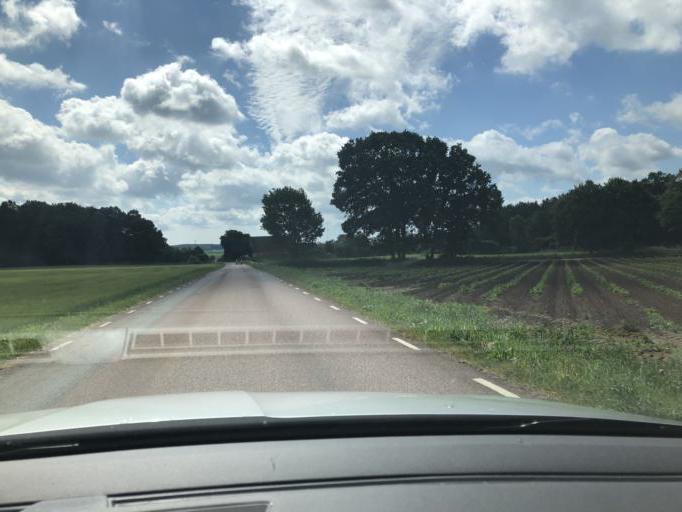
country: SE
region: Blekinge
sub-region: Solvesborgs Kommun
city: Soelvesborg
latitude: 56.1219
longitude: 14.6168
